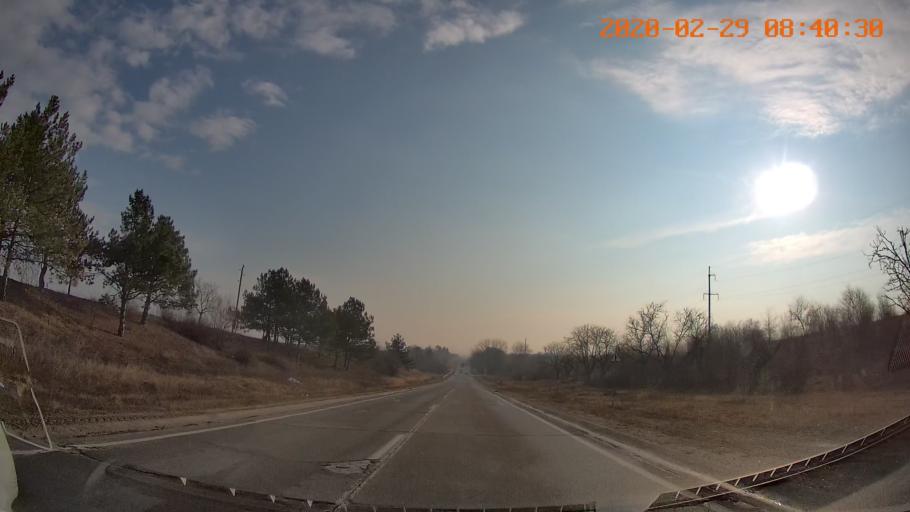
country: MD
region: Anenii Noi
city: Varnita
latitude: 46.9234
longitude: 29.4190
